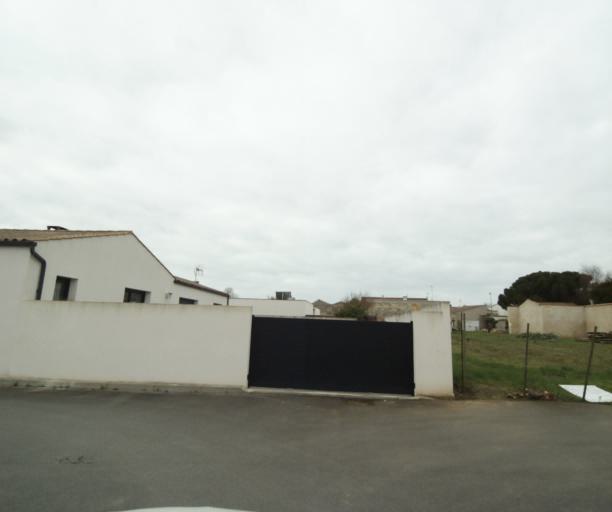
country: FR
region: Poitou-Charentes
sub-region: Departement de la Charente-Maritime
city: Lagord
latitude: 46.1925
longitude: -1.1513
